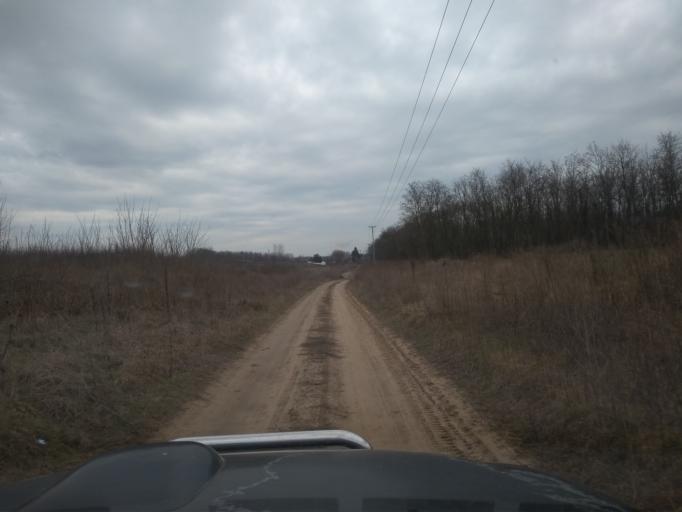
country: HU
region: Szabolcs-Szatmar-Bereg
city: Nyirpazony
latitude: 48.0156
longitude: 21.7886
